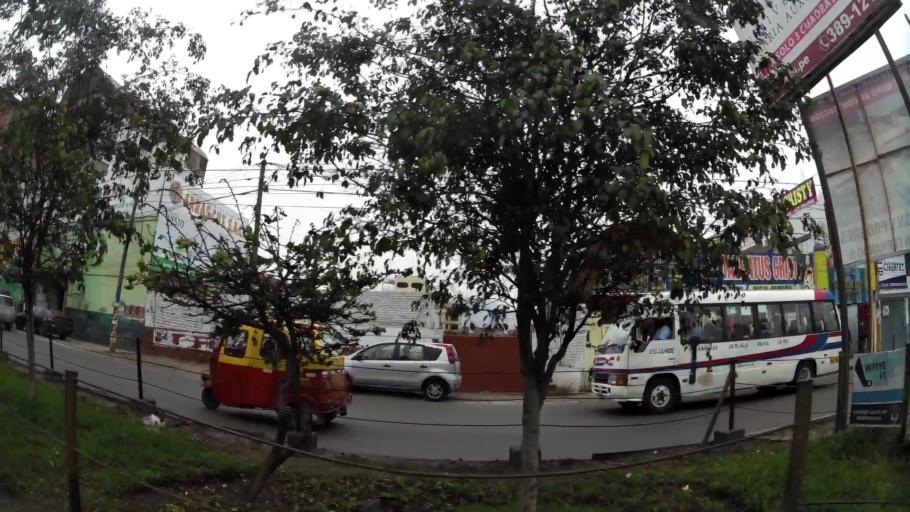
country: PE
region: Lima
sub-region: Lima
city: Independencia
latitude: -11.9808
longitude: -77.0124
